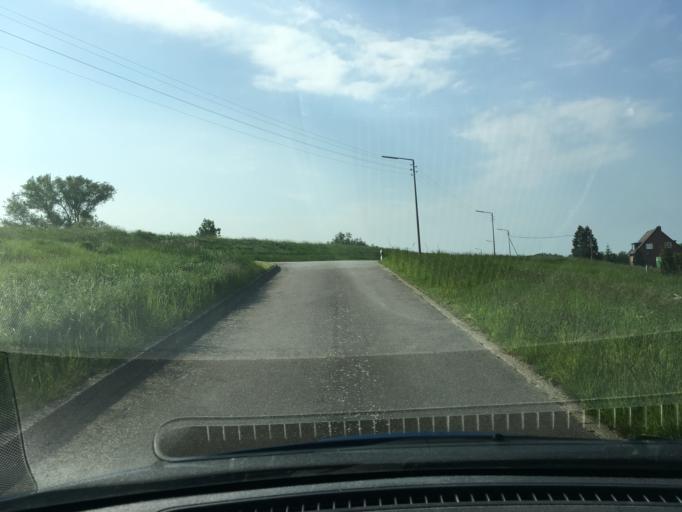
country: DE
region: Hamburg
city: Rothenburgsort
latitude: 53.4690
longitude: 10.0519
